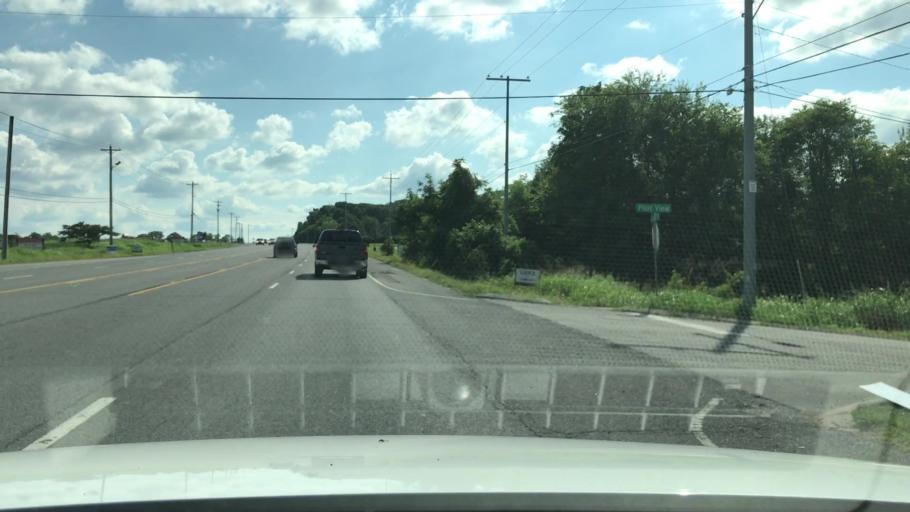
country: US
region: Tennessee
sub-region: Sumner County
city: Shackle Island
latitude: 36.3444
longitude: -86.5285
